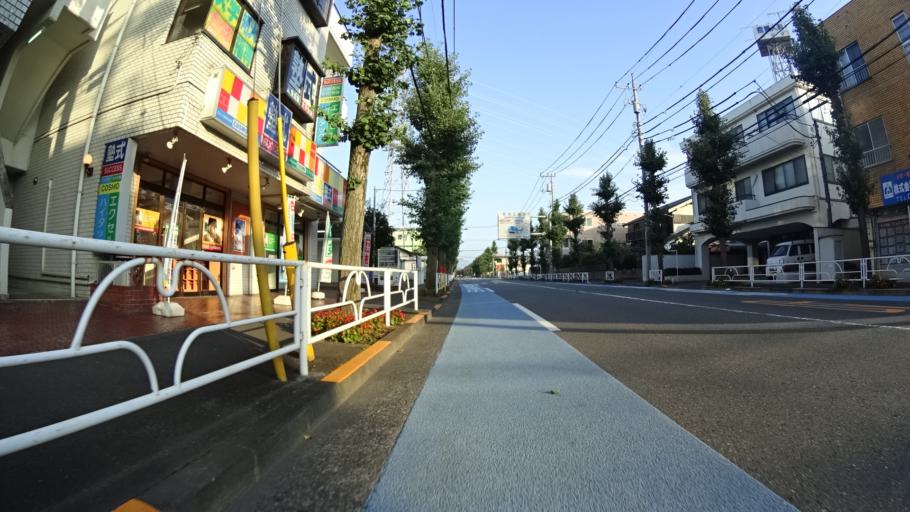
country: JP
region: Tokyo
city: Fussa
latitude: 35.7740
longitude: 139.3011
